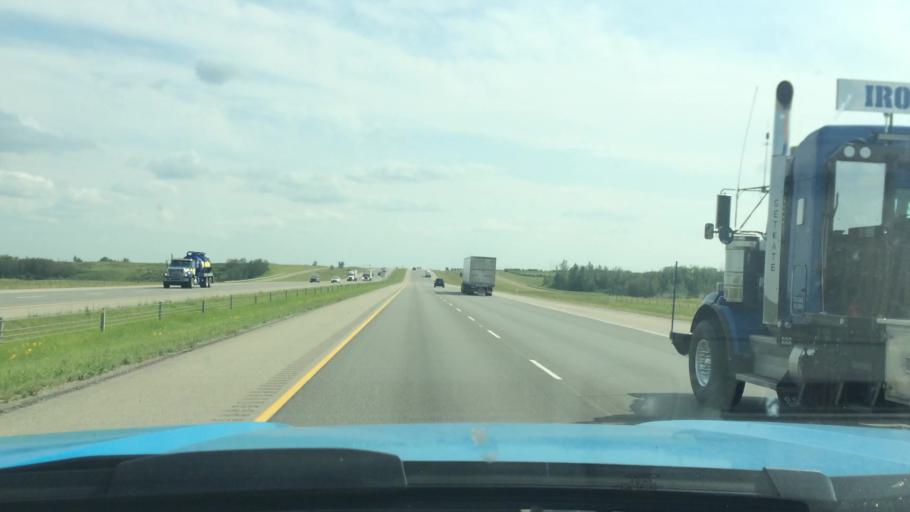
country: CA
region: Alberta
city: Crossfield
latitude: 51.5194
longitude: -114.0262
